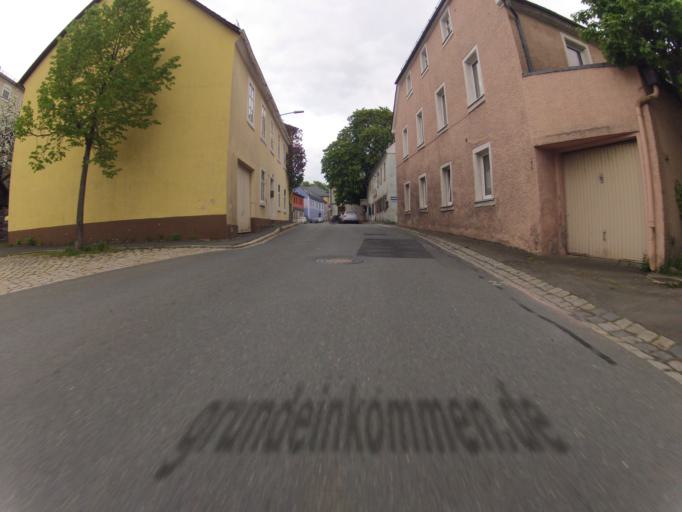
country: DE
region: Bavaria
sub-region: Upper Franconia
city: Sparneck
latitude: 50.1620
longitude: 11.8435
